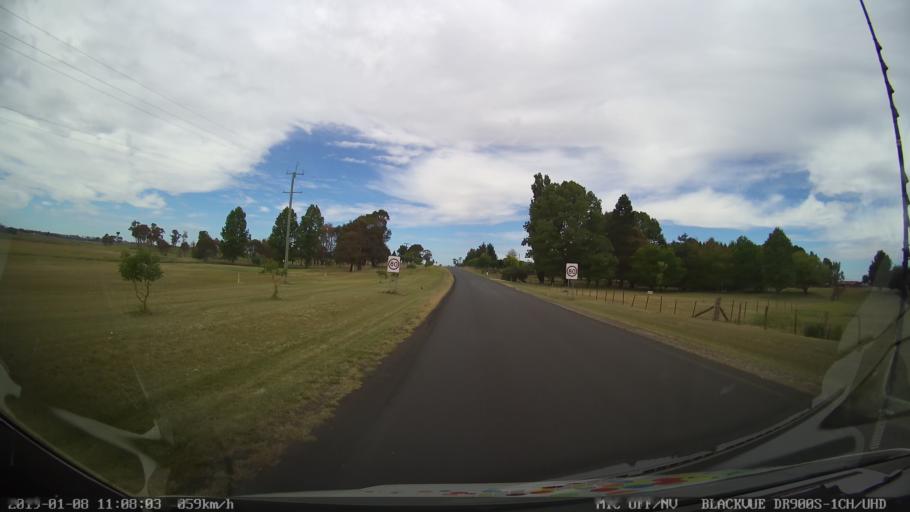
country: AU
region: New South Wales
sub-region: Guyra
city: Guyra
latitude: -30.2188
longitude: 151.6606
